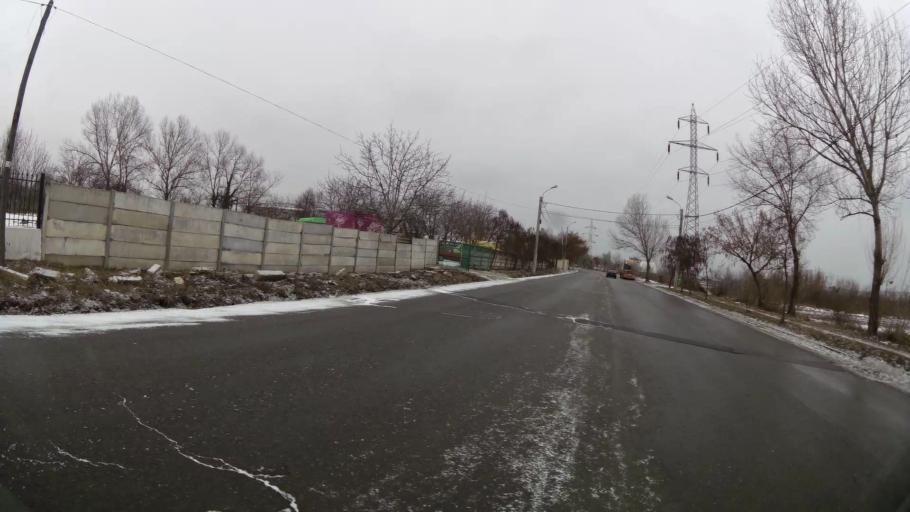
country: RO
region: Dambovita
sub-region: Municipiul Targoviste
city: Targoviste
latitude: 44.9305
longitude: 25.4764
